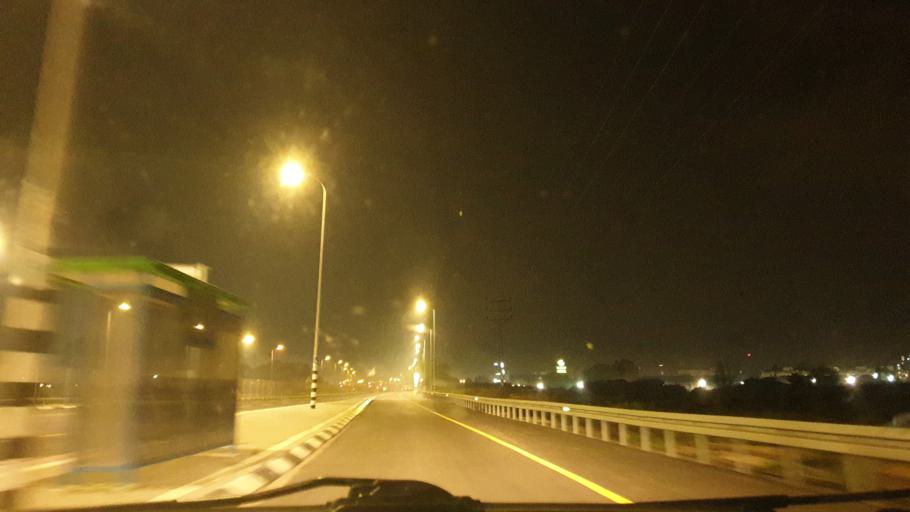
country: IL
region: Central District
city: Kefar Habad
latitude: 31.9734
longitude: 34.8410
